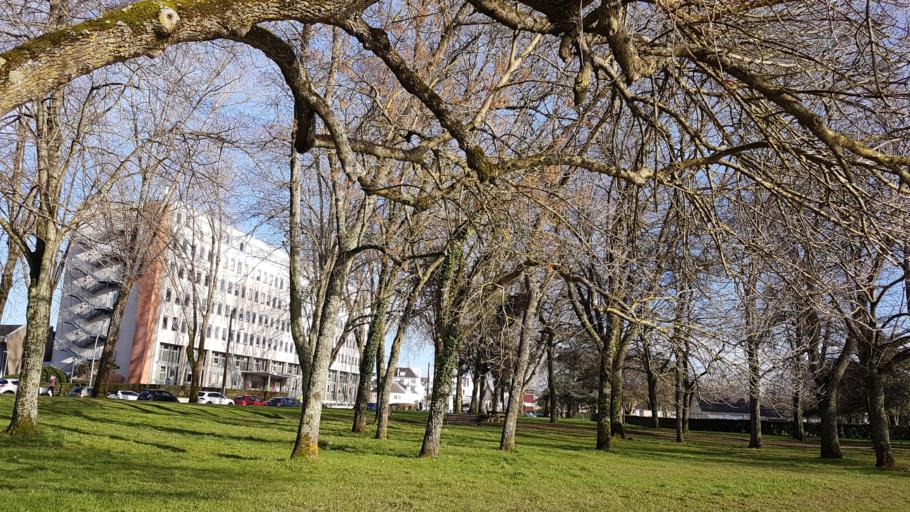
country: FR
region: Pays de la Loire
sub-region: Departement de la Loire-Atlantique
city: Saint-Nazaire
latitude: 47.2736
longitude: -2.2250
